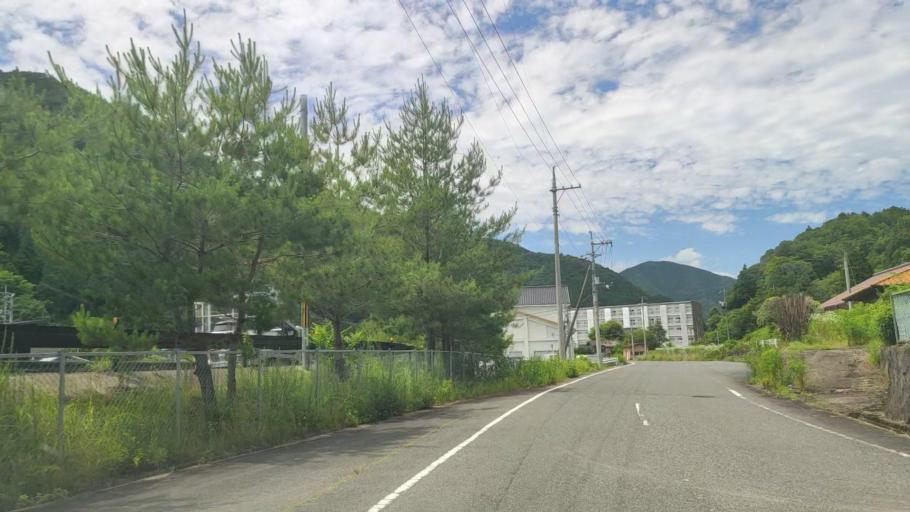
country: JP
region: Hyogo
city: Yamazakicho-nakabirose
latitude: 35.1080
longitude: 134.3283
